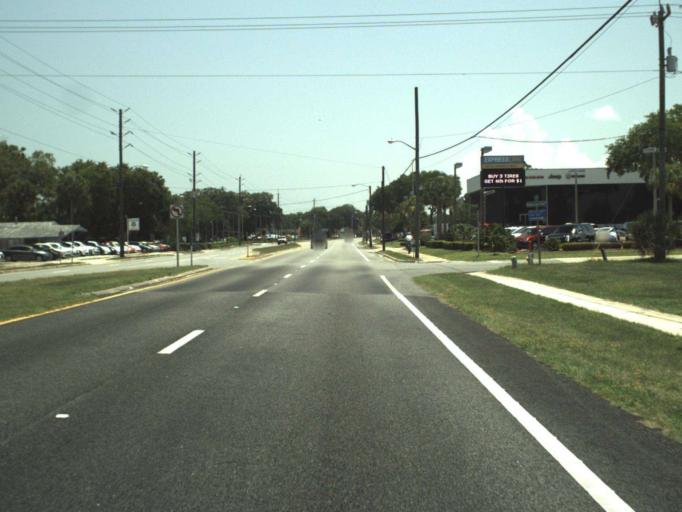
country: US
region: Florida
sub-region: Volusia County
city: New Smyrna Beach
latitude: 29.0491
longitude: -80.9368
